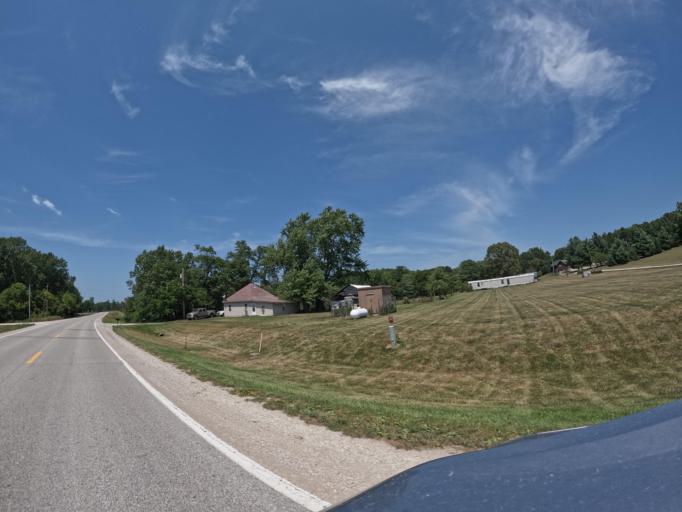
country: US
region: Iowa
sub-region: Henry County
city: Mount Pleasant
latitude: 40.9376
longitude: -91.6119
